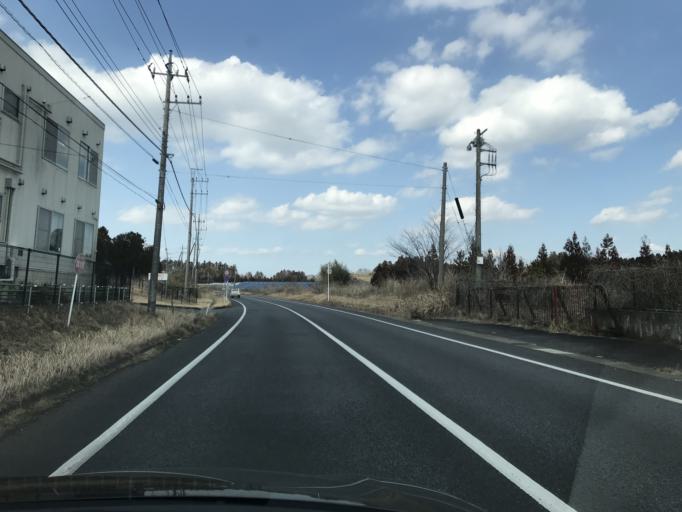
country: JP
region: Chiba
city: Sawara
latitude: 35.8195
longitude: 140.5189
